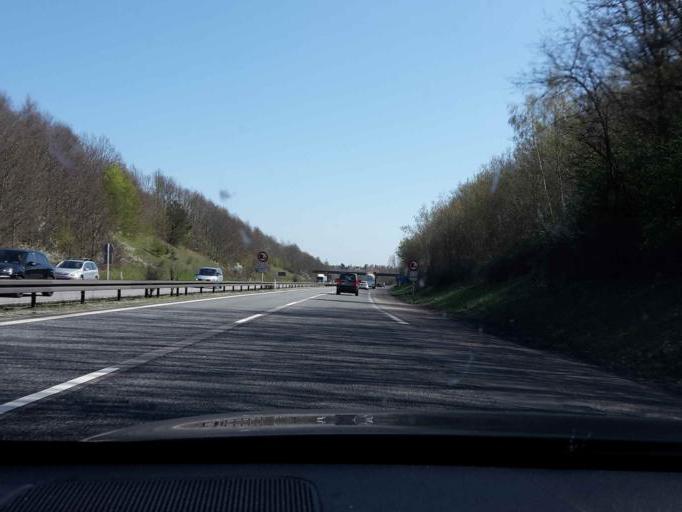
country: DK
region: South Denmark
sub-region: Odense Kommune
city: Bellinge
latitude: 55.3591
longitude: 10.3532
